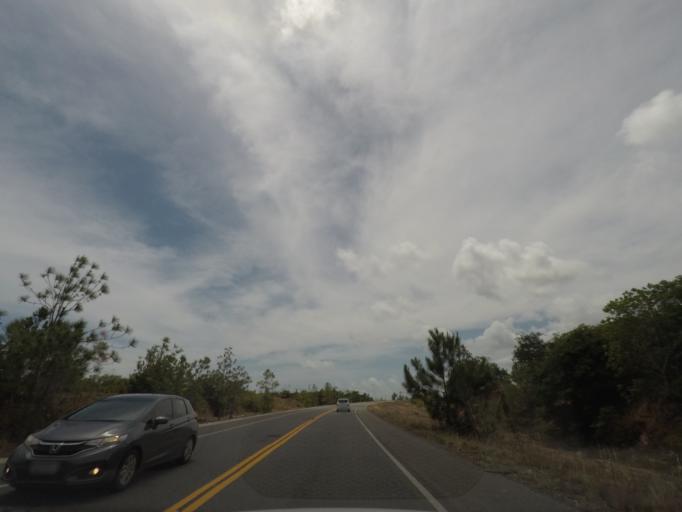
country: BR
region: Bahia
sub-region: Conde
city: Conde
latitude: -11.8673
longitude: -37.6318
